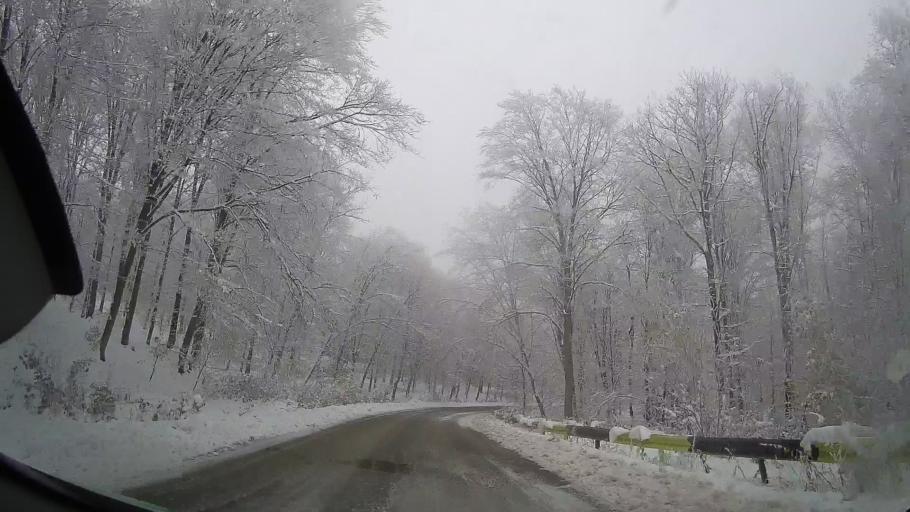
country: RO
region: Neamt
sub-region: Comuna Valea Ursului
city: Valea Ursului
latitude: 46.8389
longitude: 27.0691
